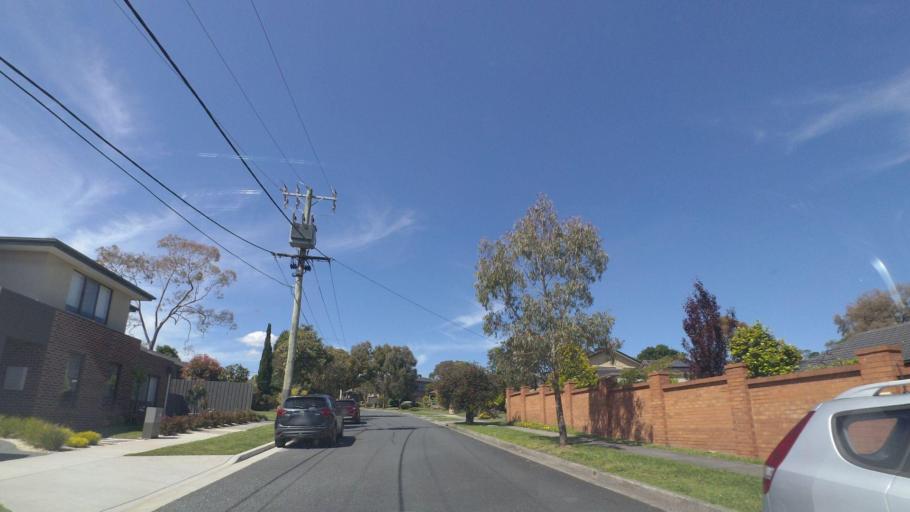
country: AU
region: Victoria
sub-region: Whitehorse
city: Vermont South
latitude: -37.8546
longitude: 145.1974
